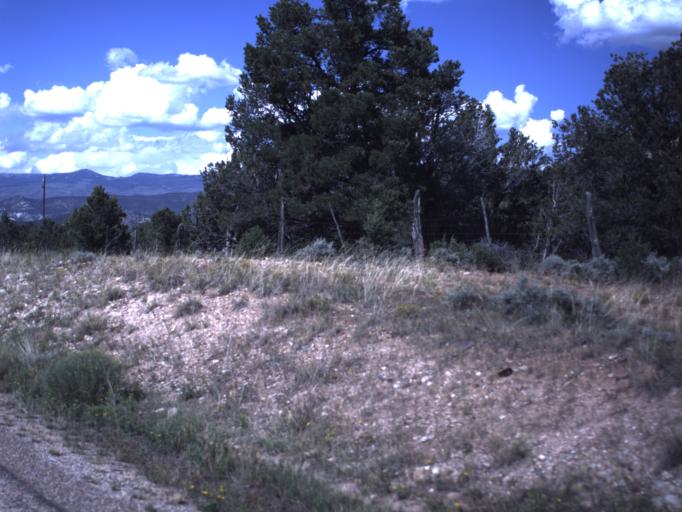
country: US
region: Utah
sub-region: Duchesne County
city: Duchesne
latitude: 40.3092
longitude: -110.6981
